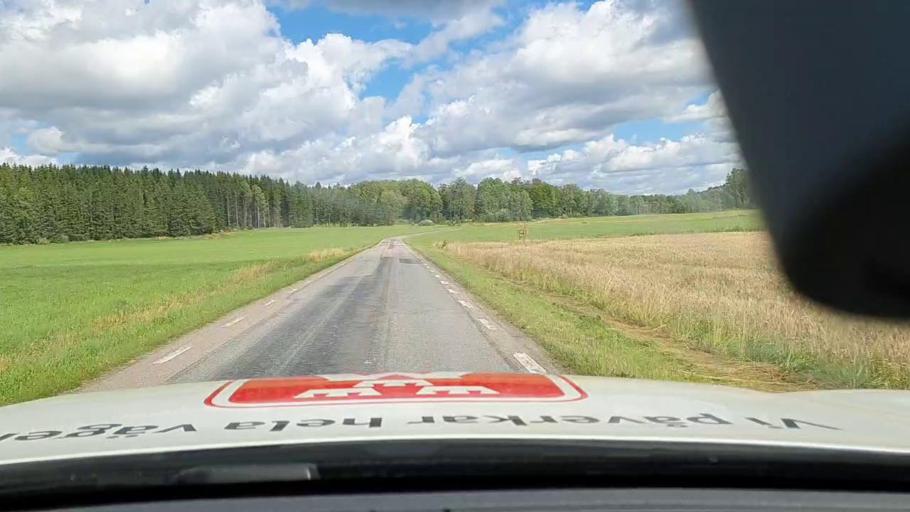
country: SE
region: Vaestra Goetaland
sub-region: Karlsborgs Kommun
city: Molltorp
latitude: 58.6098
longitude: 14.3244
